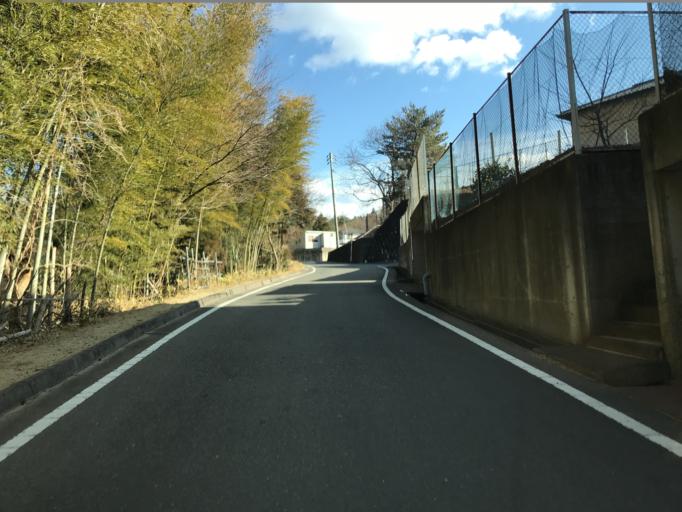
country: JP
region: Fukushima
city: Iwaki
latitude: 37.1253
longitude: 140.8430
